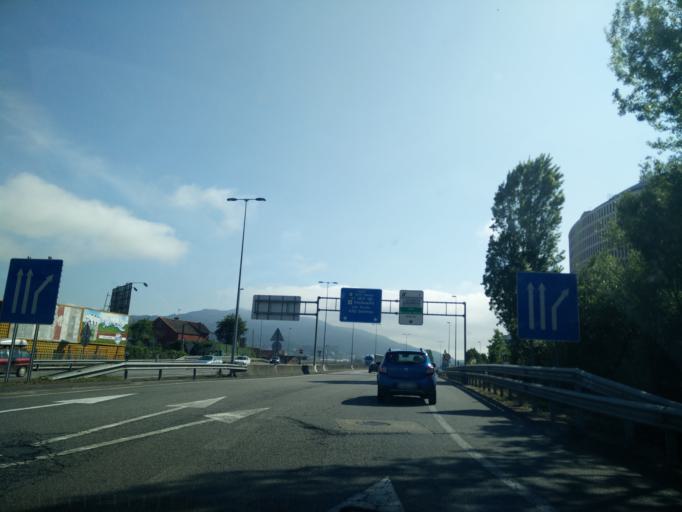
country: ES
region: Galicia
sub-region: Provincia de Pontevedra
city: Vigo
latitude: 42.2105
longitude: -8.7531
